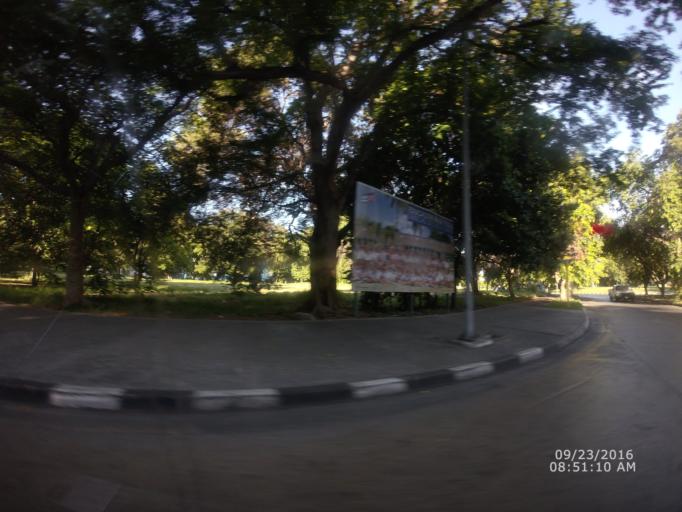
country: CU
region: La Habana
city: Havana
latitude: 23.1205
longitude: -82.3887
